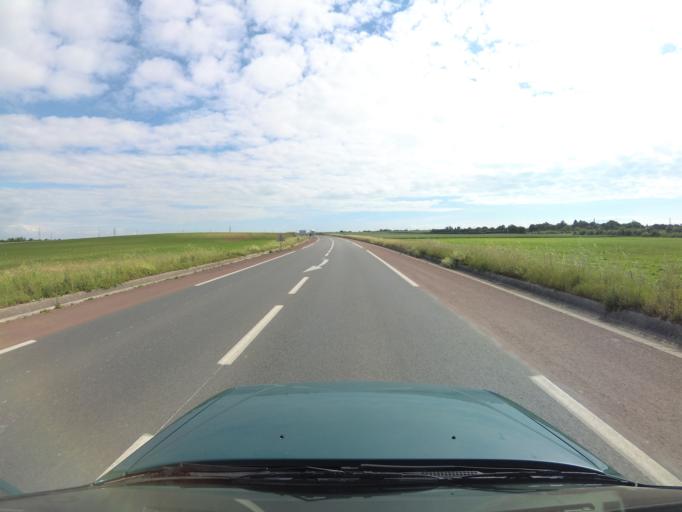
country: FR
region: Poitou-Charentes
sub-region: Departement de la Charente-Maritime
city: Saint-Xandre
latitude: 46.2158
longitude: -1.0904
